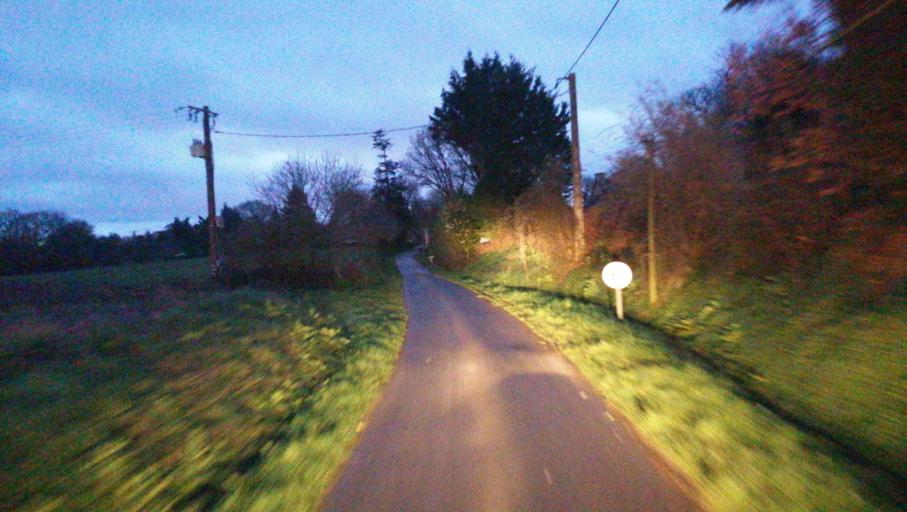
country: FR
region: Brittany
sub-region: Departement des Cotes-d'Armor
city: Plehedel
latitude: 48.6748
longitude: -3.0365
